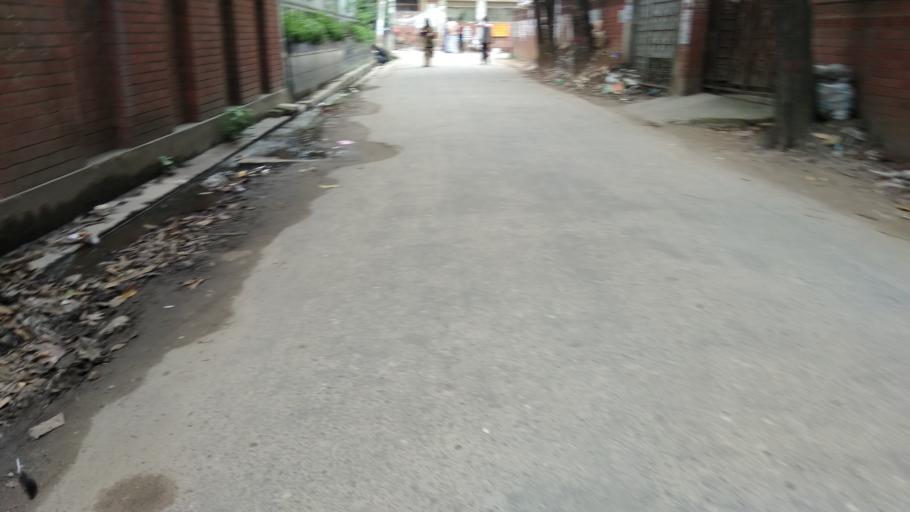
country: BD
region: Dhaka
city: Tungi
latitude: 23.8224
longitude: 90.3613
